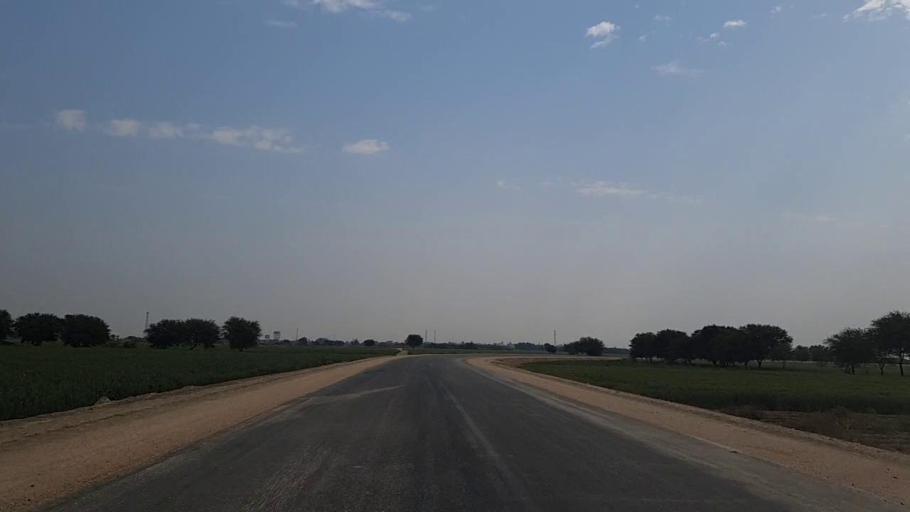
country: PK
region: Sindh
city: Naukot
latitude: 24.9804
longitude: 69.2861
